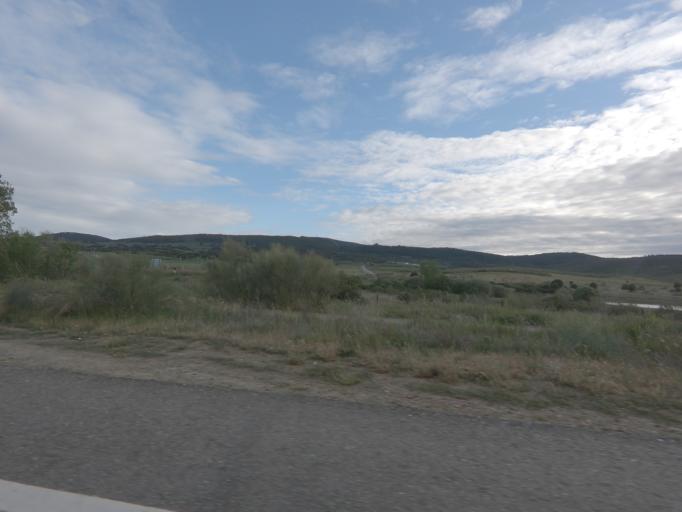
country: ES
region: Extremadura
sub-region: Provincia de Caceres
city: Pedroso de Acim
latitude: 39.8417
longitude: -6.4016
